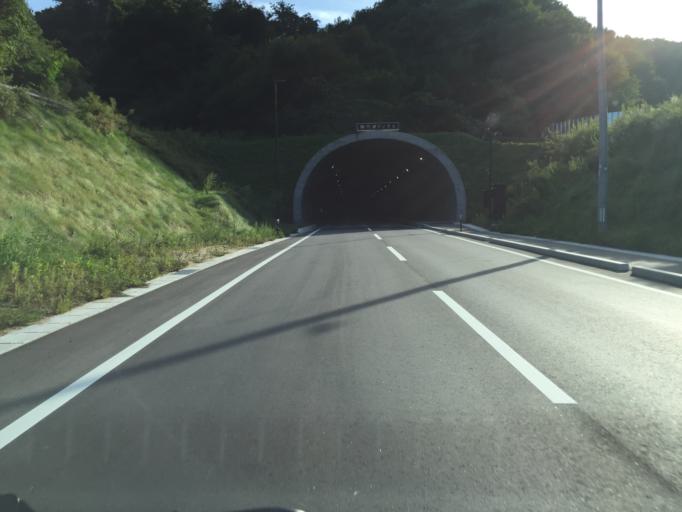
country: JP
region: Fukushima
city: Hobaramachi
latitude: 37.7389
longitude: 140.6070
